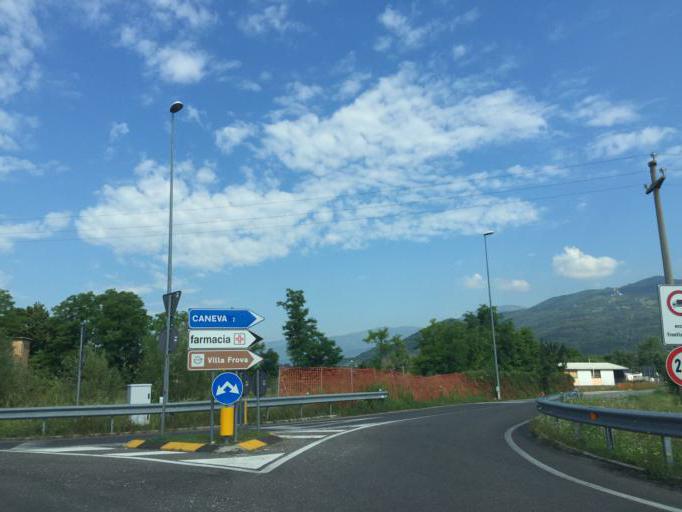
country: IT
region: Friuli Venezia Giulia
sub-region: Provincia di Pordenone
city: Caneva
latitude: 45.9563
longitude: 12.4485
